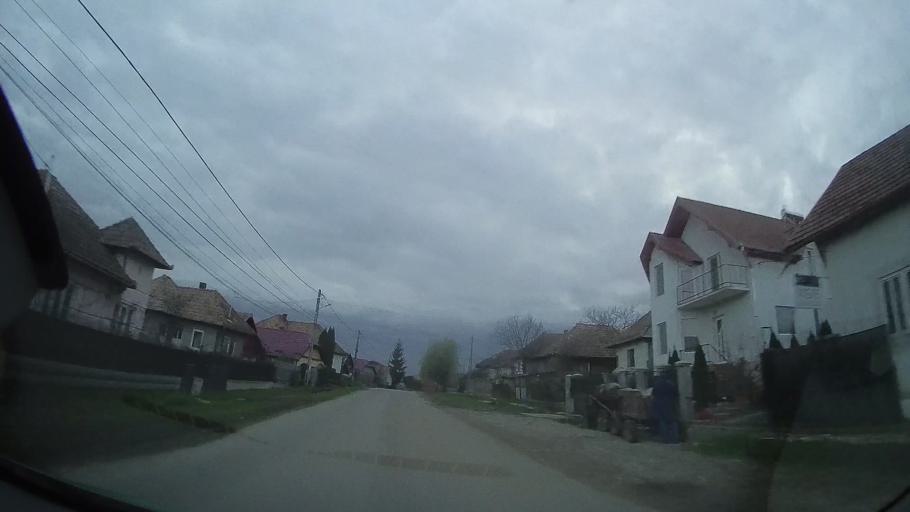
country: RO
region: Cluj
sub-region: Comuna Caianu
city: Vaida-Camaras
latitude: 46.8246
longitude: 23.9420
